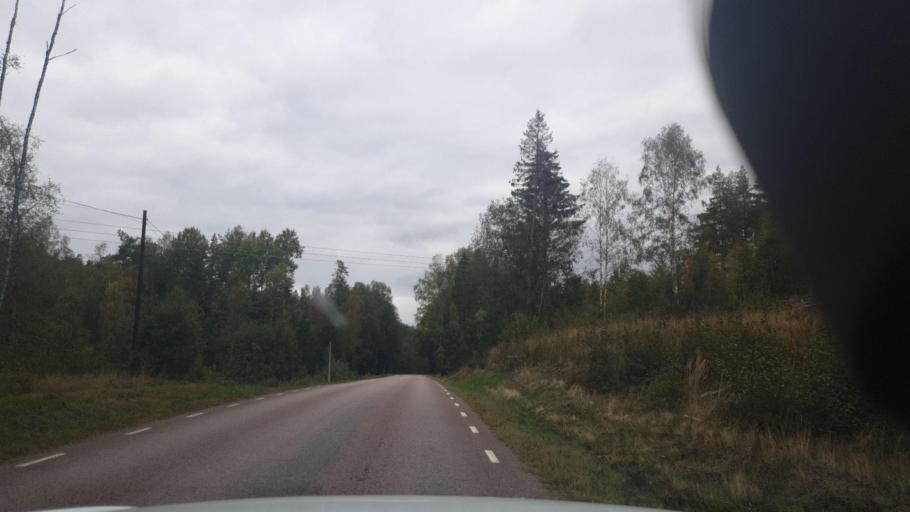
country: SE
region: Vaermland
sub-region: Grums Kommun
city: Grums
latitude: 59.4054
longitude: 13.0715
